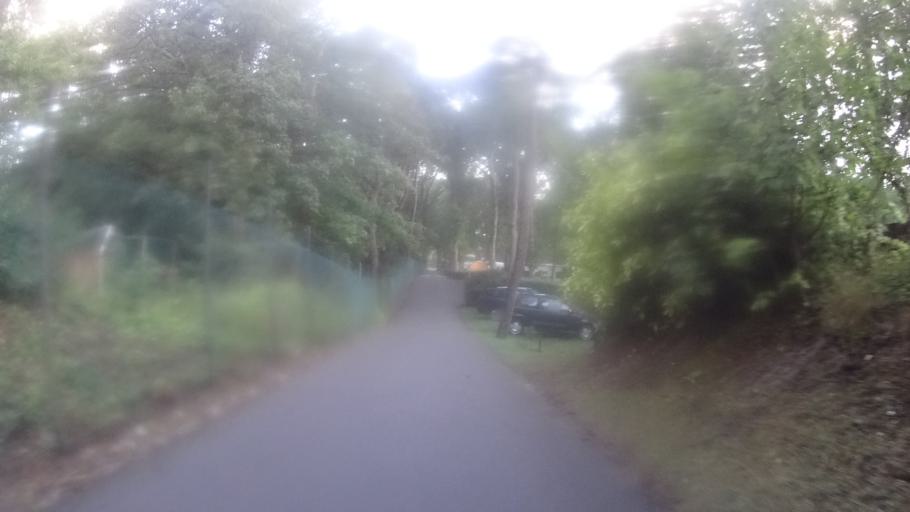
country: NL
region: South Holland
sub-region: Gemeente Leidschendam-Voorburg
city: Voorburg
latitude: 52.1093
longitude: 4.3449
